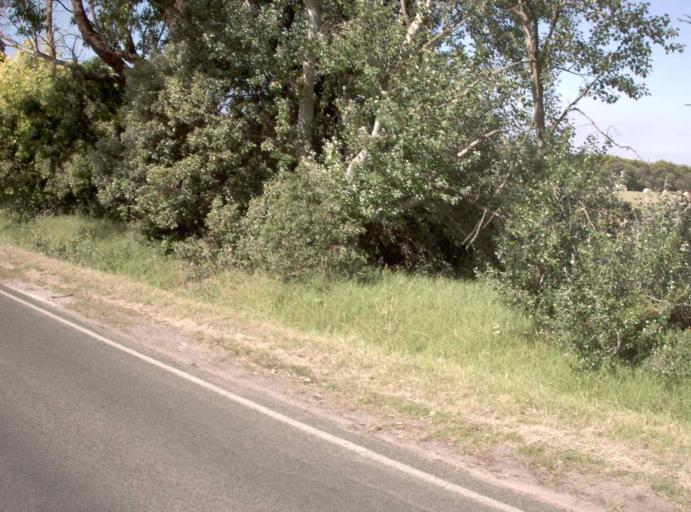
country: AU
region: Victoria
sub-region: Latrobe
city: Traralgon
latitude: -38.5741
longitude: 146.6736
